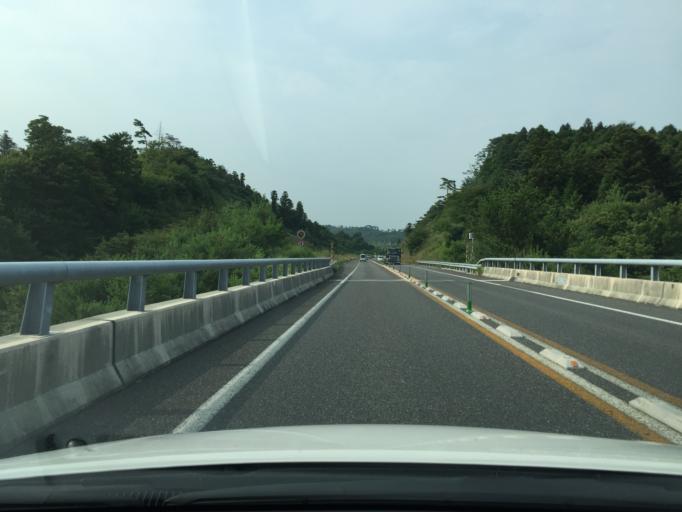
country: JP
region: Fukushima
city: Iwaki
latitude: 37.1602
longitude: 140.9665
